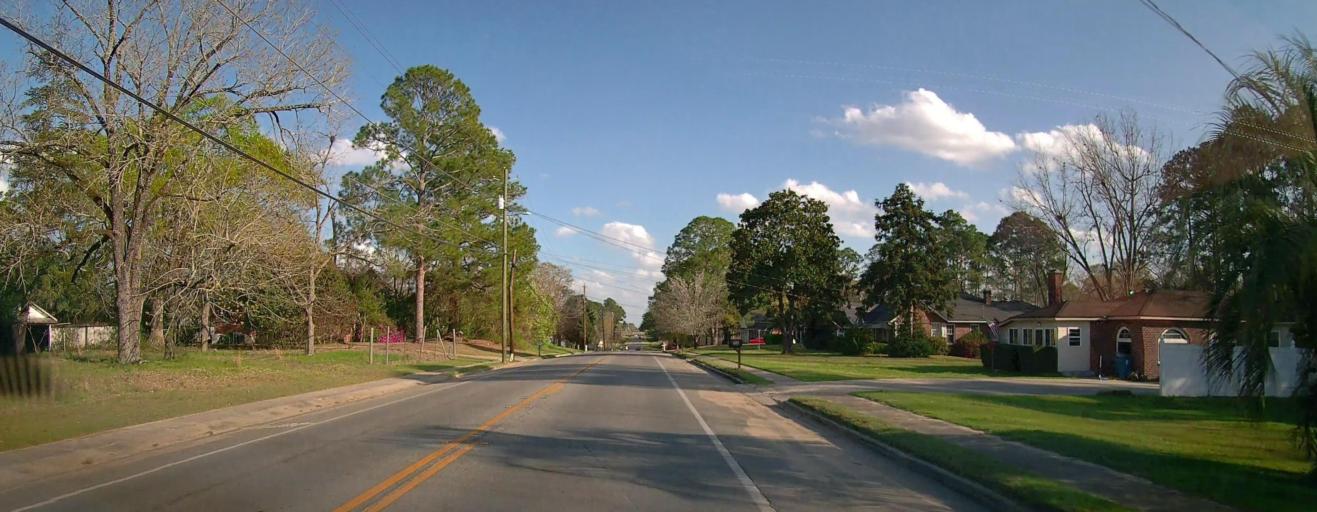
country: US
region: Georgia
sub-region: Toombs County
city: Lyons
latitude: 32.2021
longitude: -82.3179
